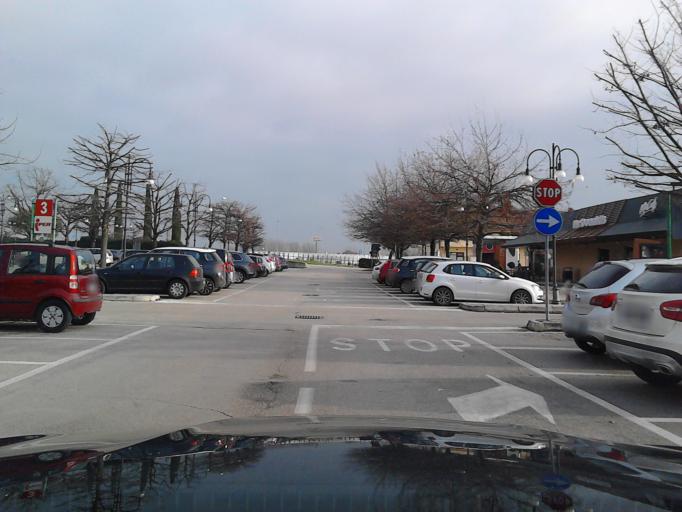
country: IT
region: Abruzzo
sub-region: Provincia di Teramo
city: Villa Rosa
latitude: 42.8363
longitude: 13.8931
